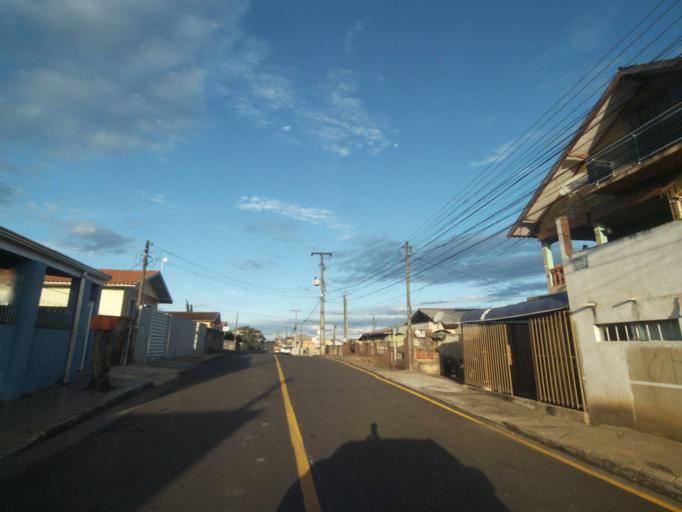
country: BR
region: Parana
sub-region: Telemaco Borba
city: Telemaco Borba
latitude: -24.3245
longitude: -50.6399
